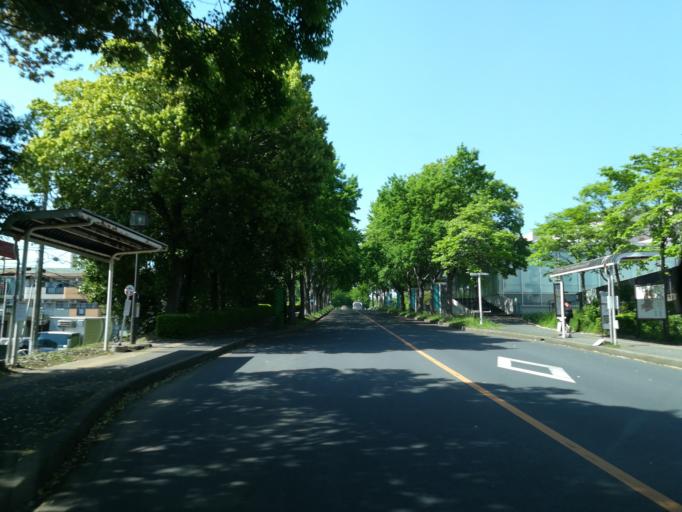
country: JP
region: Ibaraki
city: Naka
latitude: 36.1046
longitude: 140.1013
